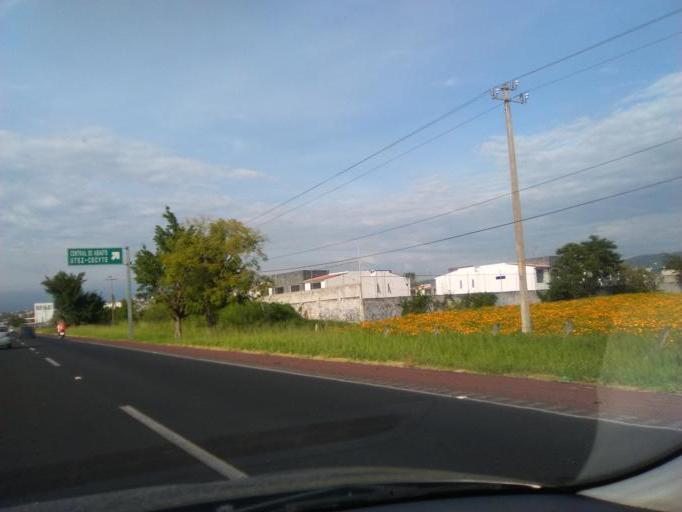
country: MX
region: Morelos
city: Temixco
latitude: 18.8229
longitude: -99.2185
